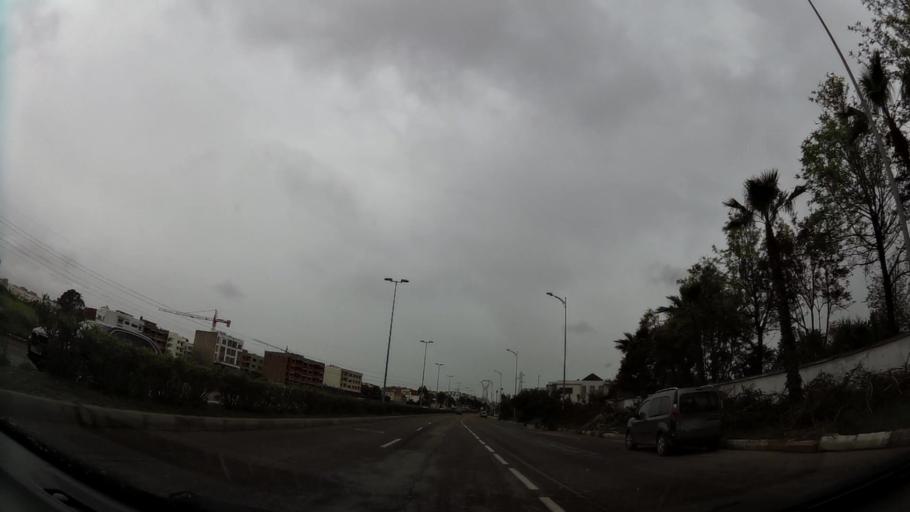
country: MA
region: Grand Casablanca
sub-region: Casablanca
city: Casablanca
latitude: 33.5397
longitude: -7.6181
